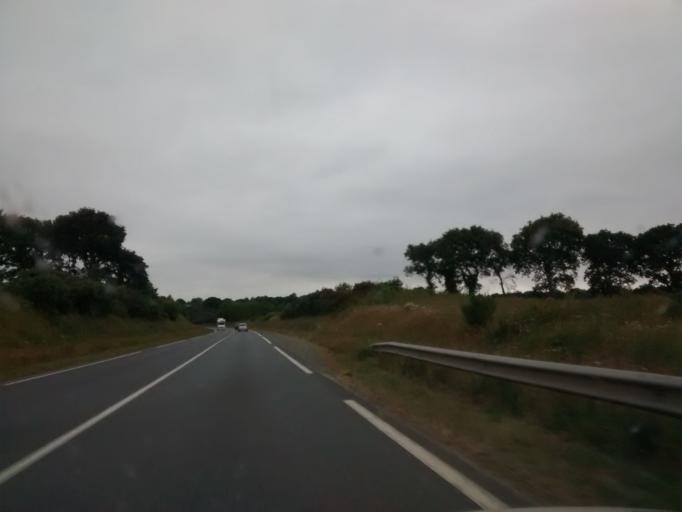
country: FR
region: Brittany
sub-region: Departement des Cotes-d'Armor
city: Lannion
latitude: 48.7382
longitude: -3.4391
